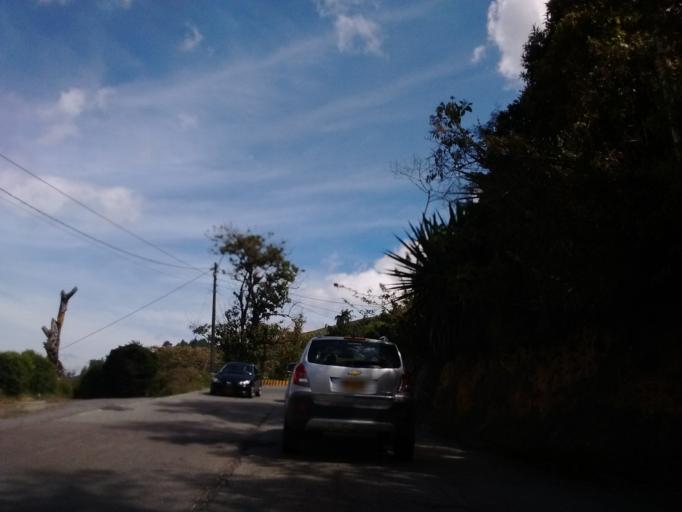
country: CO
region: Antioquia
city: Medellin
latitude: 6.2437
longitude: -75.5140
